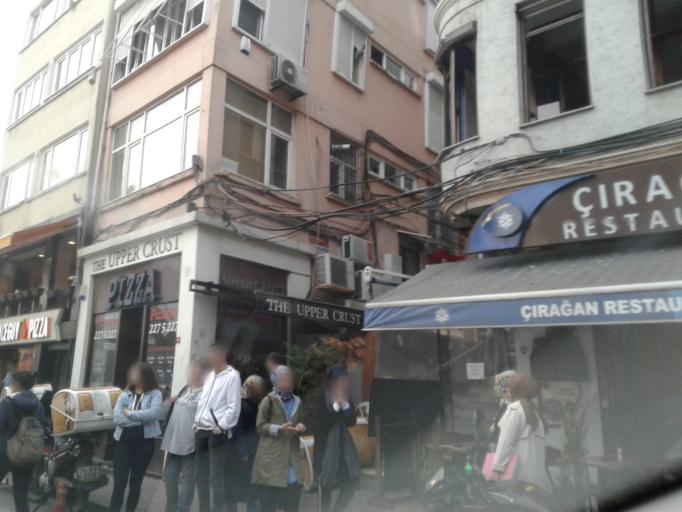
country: TR
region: Istanbul
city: UEskuedar
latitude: 41.0429
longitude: 29.0101
